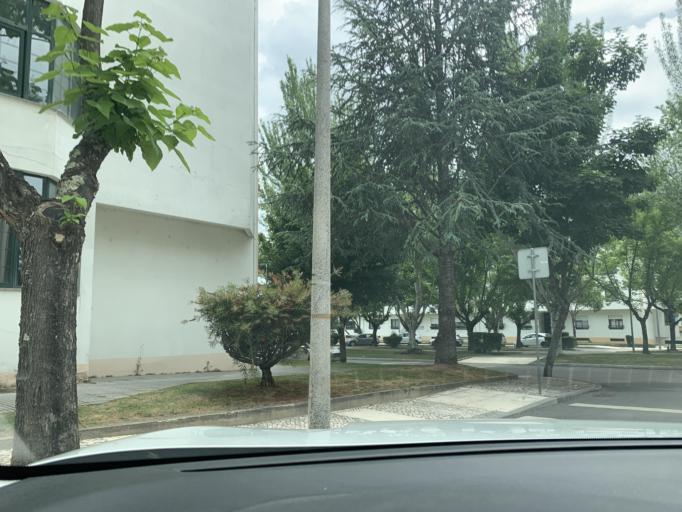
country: PT
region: Viseu
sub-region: Viseu
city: Rio de Loba
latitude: 40.6487
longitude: -7.8897
